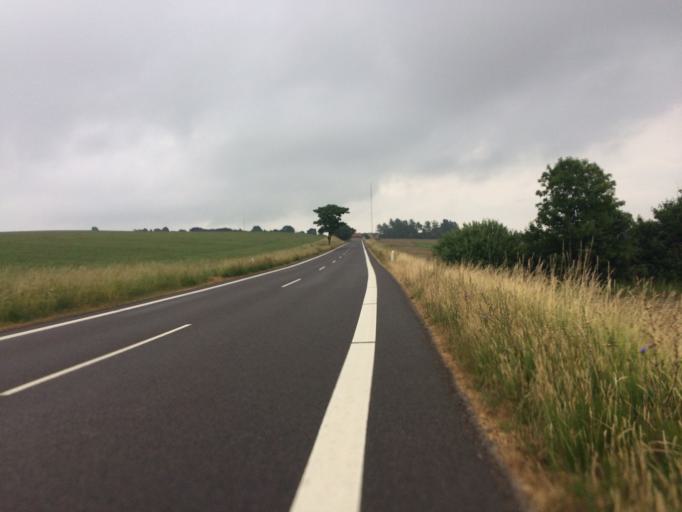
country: DK
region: Capital Region
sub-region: Bornholm Kommune
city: Akirkeby
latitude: 55.1403
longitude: 14.8605
